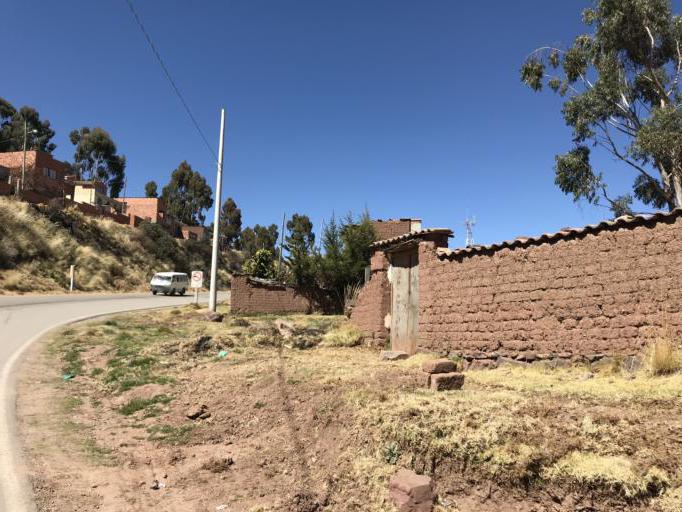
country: BO
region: La Paz
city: San Pablo
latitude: -16.2141
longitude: -68.8473
